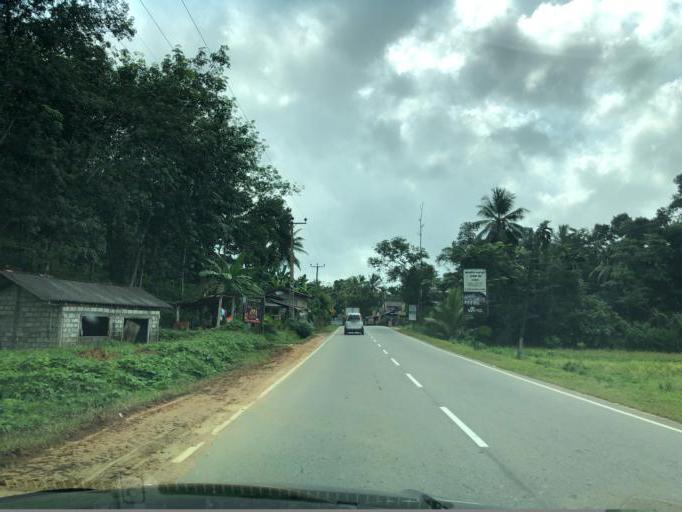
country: LK
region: Western
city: Horana South
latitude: 6.6793
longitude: 80.1513
